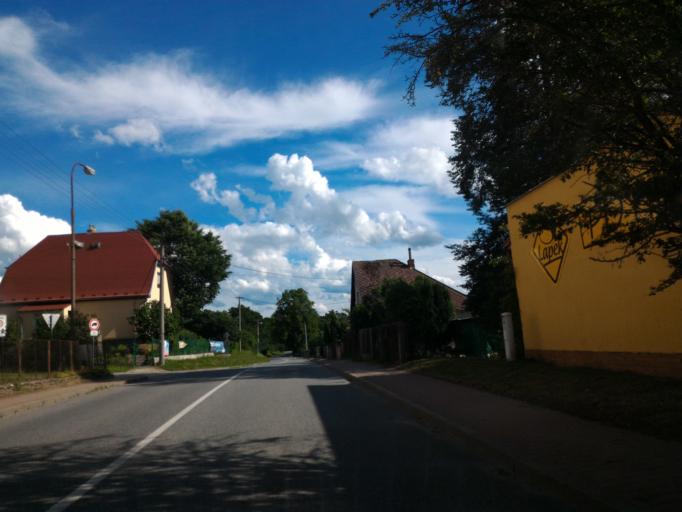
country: CZ
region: Vysocina
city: Dolni Cerekev
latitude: 49.3597
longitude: 15.4910
